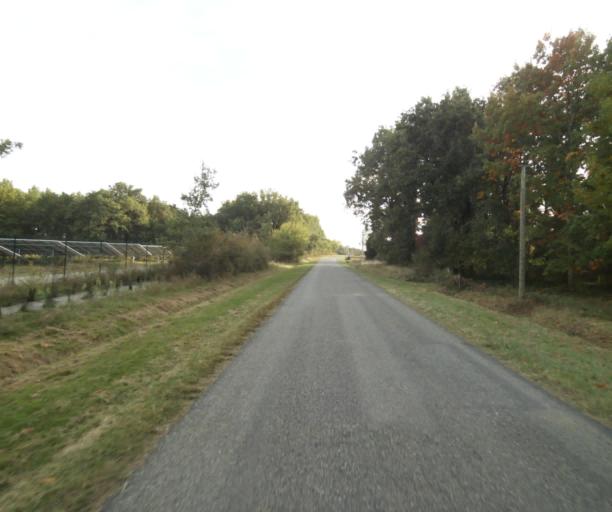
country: FR
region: Midi-Pyrenees
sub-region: Departement du Tarn-et-Garonne
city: Campsas
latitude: 43.8793
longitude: 1.3209
